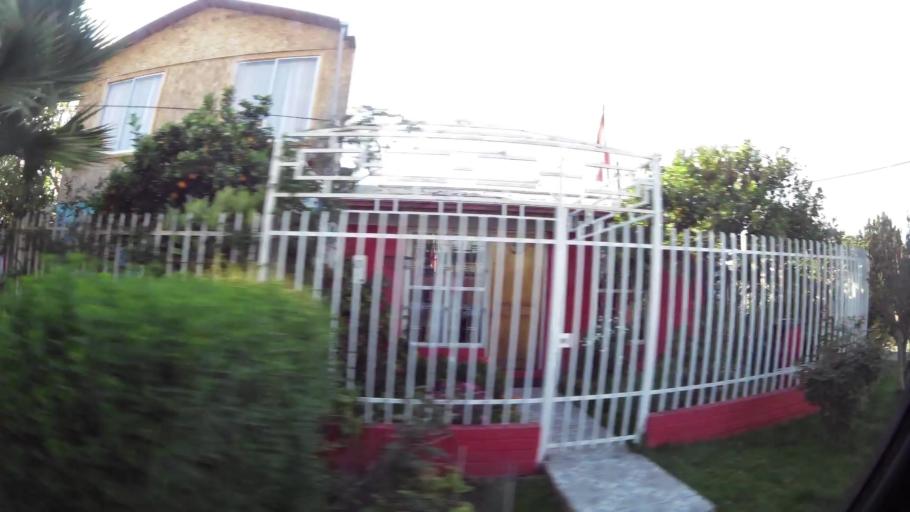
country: CL
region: Santiago Metropolitan
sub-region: Provincia de Santiago
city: Lo Prado
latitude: -33.4381
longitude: -70.7456
